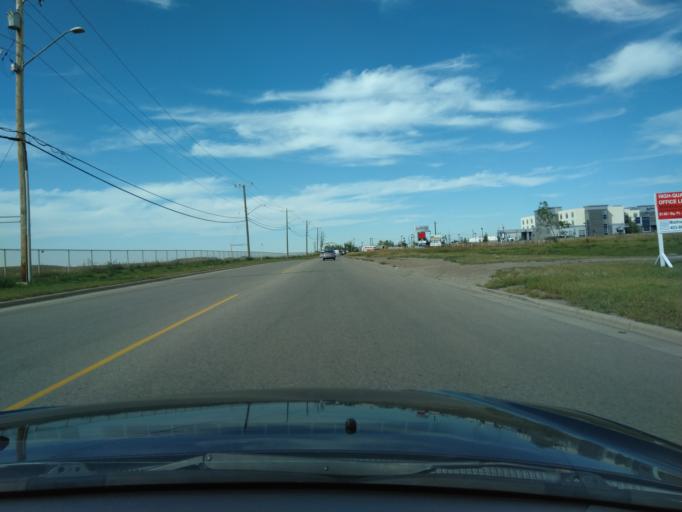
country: CA
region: Alberta
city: Calgary
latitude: 51.1099
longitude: -113.9821
